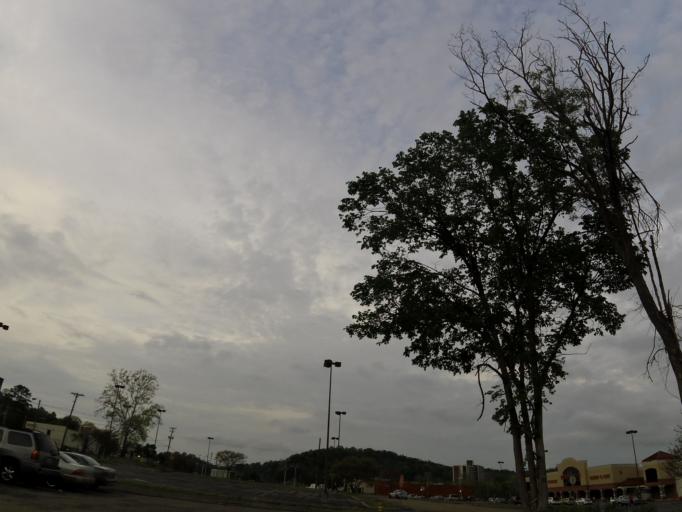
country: US
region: Tennessee
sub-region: Knox County
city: Knoxville
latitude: 36.0093
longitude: -83.9243
